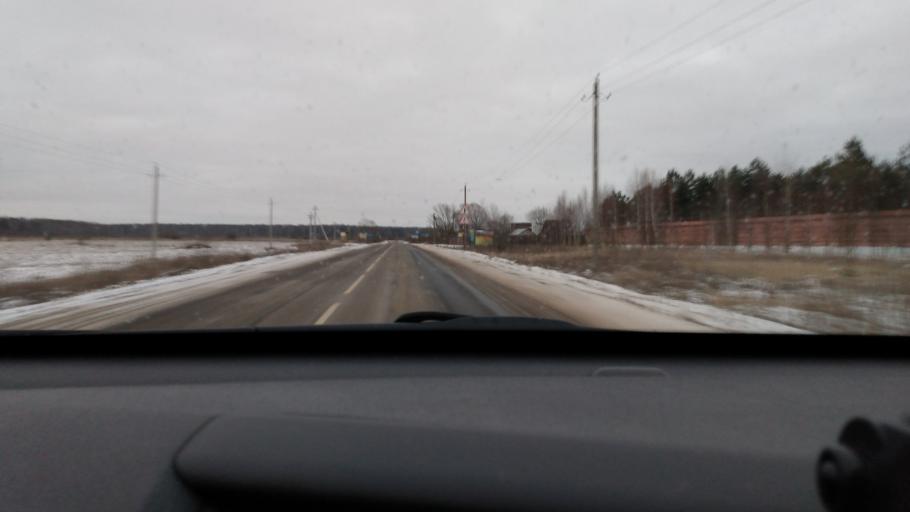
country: RU
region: Moskovskaya
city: Meshcherino
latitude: 55.2907
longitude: 38.2795
